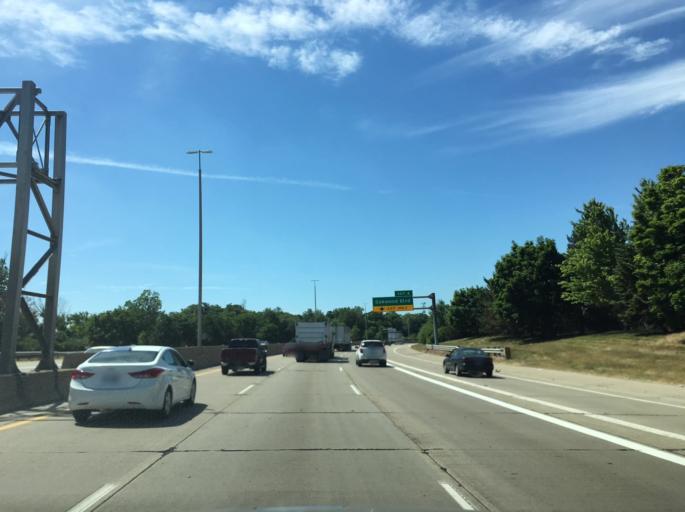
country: US
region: Michigan
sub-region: Wayne County
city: Melvindale
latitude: 42.2957
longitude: -83.2046
